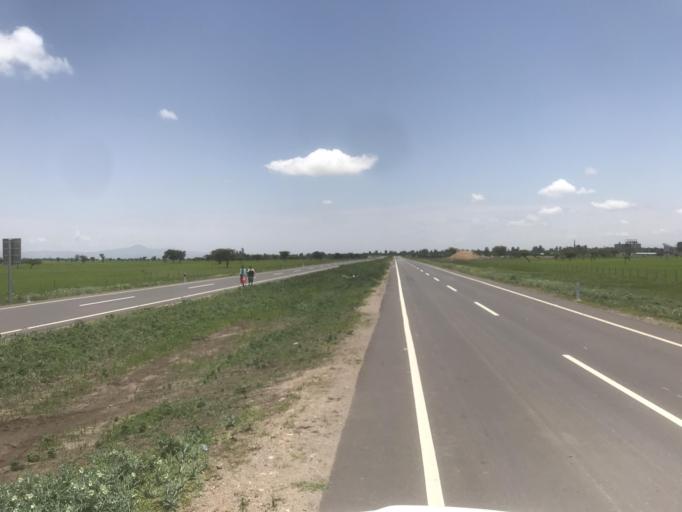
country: ET
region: Oromiya
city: Mojo
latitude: 8.5566
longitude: 39.1120
